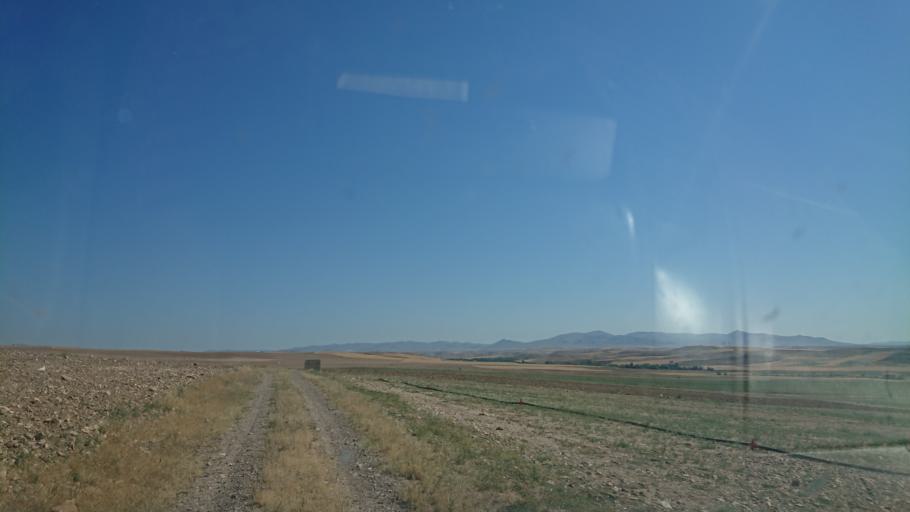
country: TR
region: Aksaray
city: Sariyahsi
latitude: 39.0468
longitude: 33.8902
